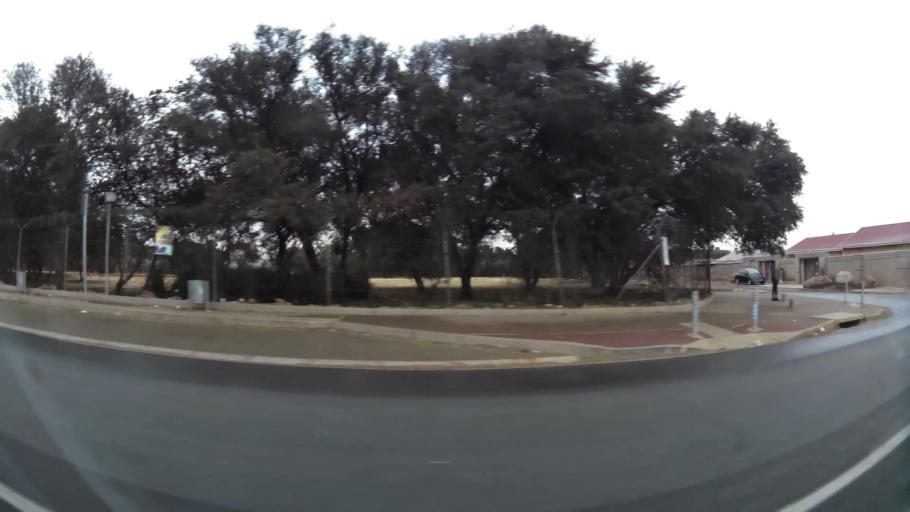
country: ZA
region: Gauteng
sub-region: City of Johannesburg Metropolitan Municipality
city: Soweto
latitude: -26.2454
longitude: 27.8679
